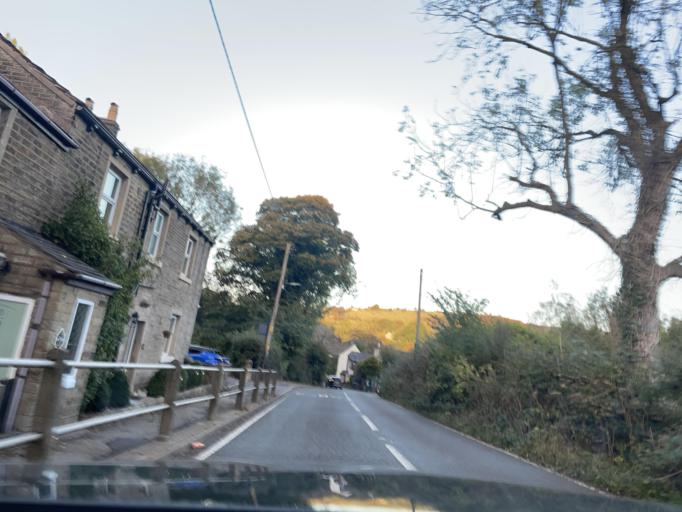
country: GB
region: England
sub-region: Borough of Tameside
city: Longdendale
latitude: 53.4267
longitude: -2.0015
